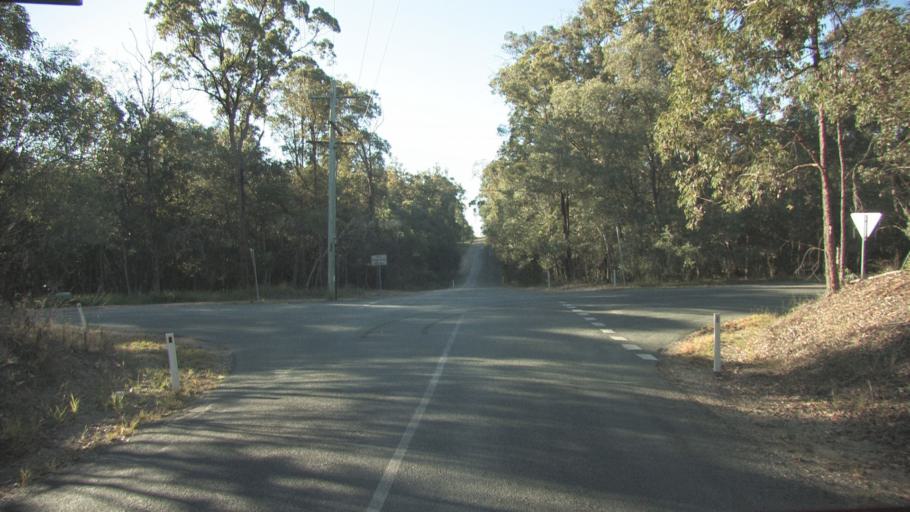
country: AU
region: Queensland
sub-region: Logan
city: Chambers Flat
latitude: -27.7615
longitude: 153.1233
